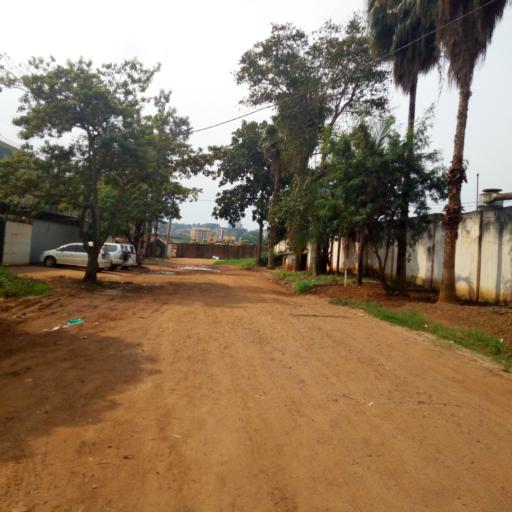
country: UG
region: Central Region
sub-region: Kampala District
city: Kampala
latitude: 0.3162
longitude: 32.6156
